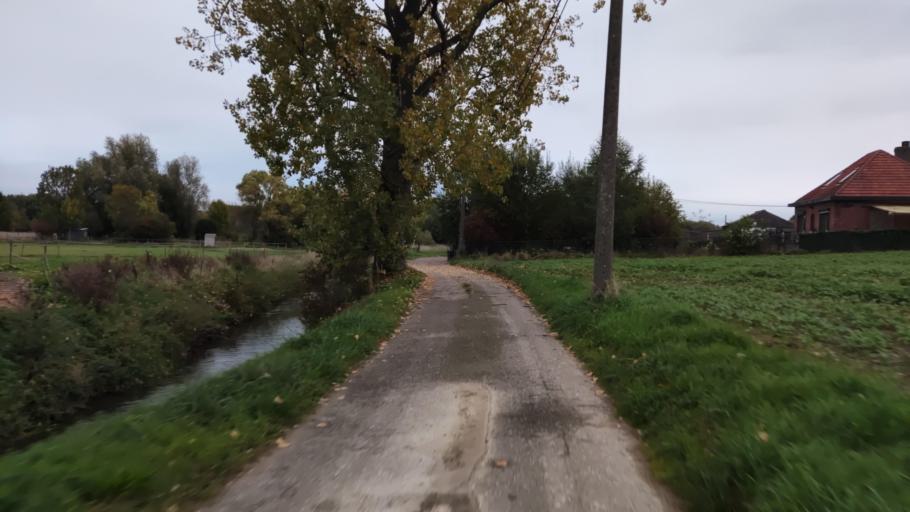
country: BE
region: Flanders
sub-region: Provincie Vlaams-Brabant
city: Hoegaarden
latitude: 50.7754
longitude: 4.8997
